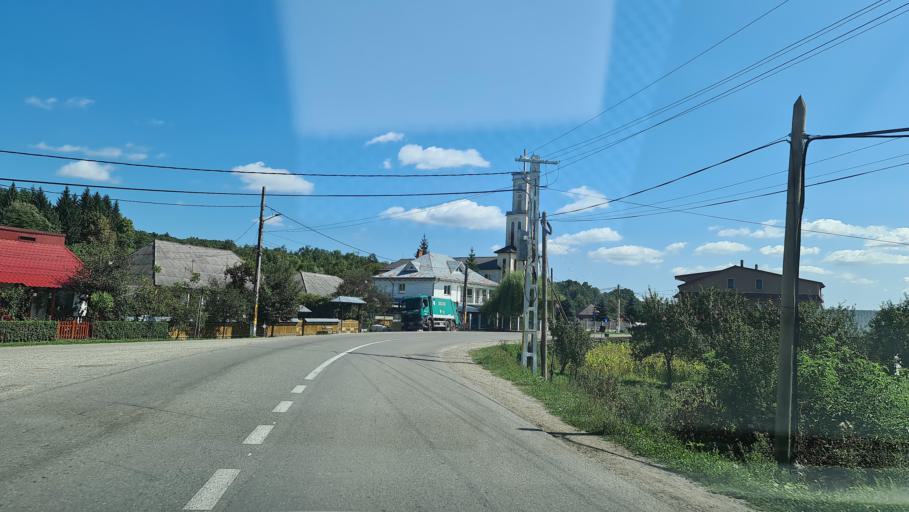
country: RO
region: Bacau
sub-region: Comuna Balcani
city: Frumoasa
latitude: 46.6636
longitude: 26.5387
